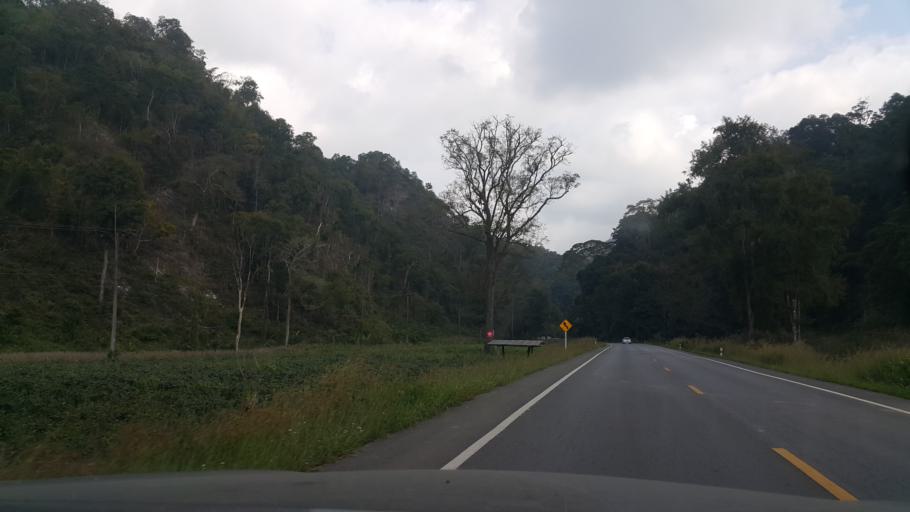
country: TH
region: Lampang
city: Wang Nuea
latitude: 19.0654
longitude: 99.7419
